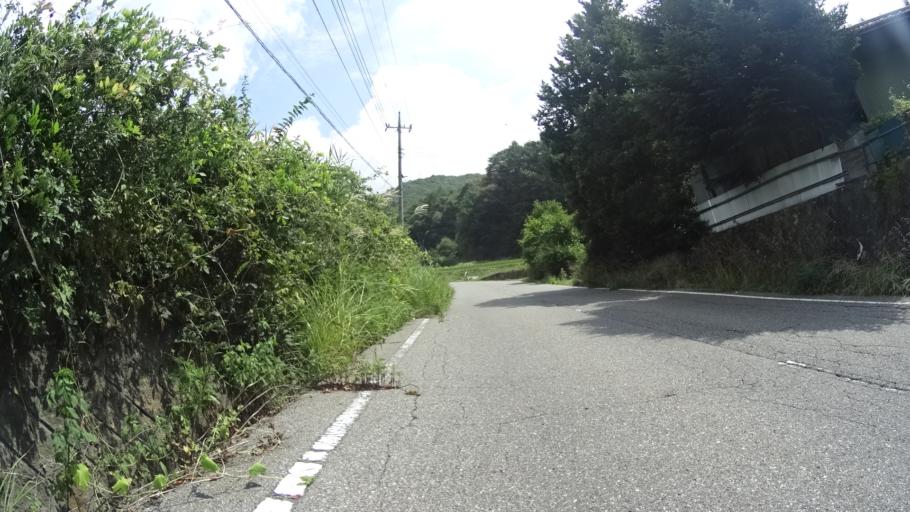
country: JP
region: Yamanashi
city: Nirasaki
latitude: 35.8777
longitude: 138.5174
